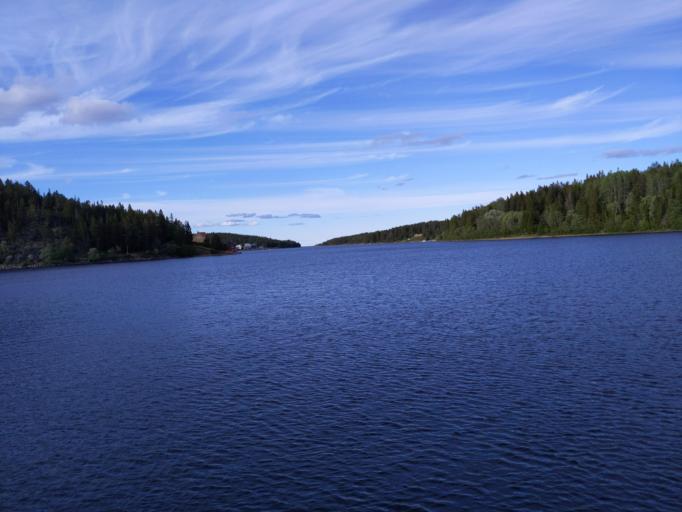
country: SE
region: Vaesternorrland
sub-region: OErnskoeldsviks Kommun
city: Kopmanholmen
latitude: 63.0147
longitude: 18.6368
